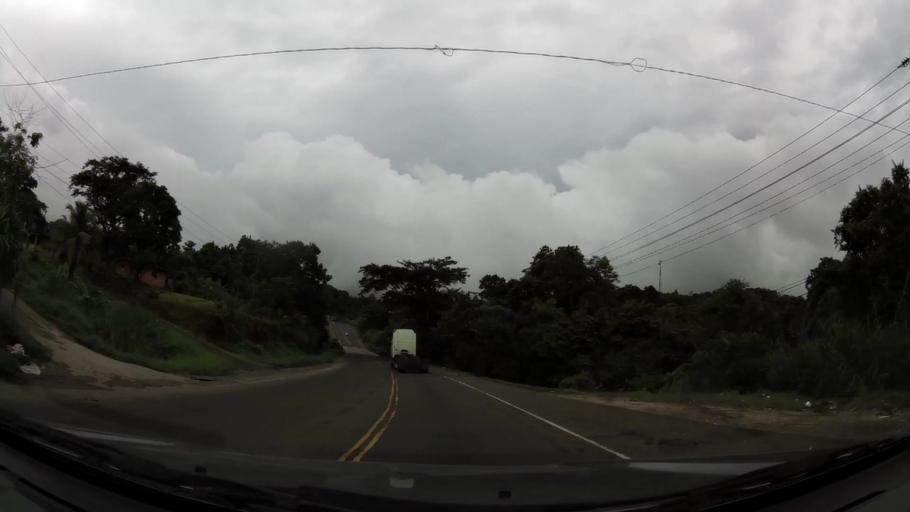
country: PA
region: Colon
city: Nuevo Vigia
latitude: 9.2379
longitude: -79.6327
